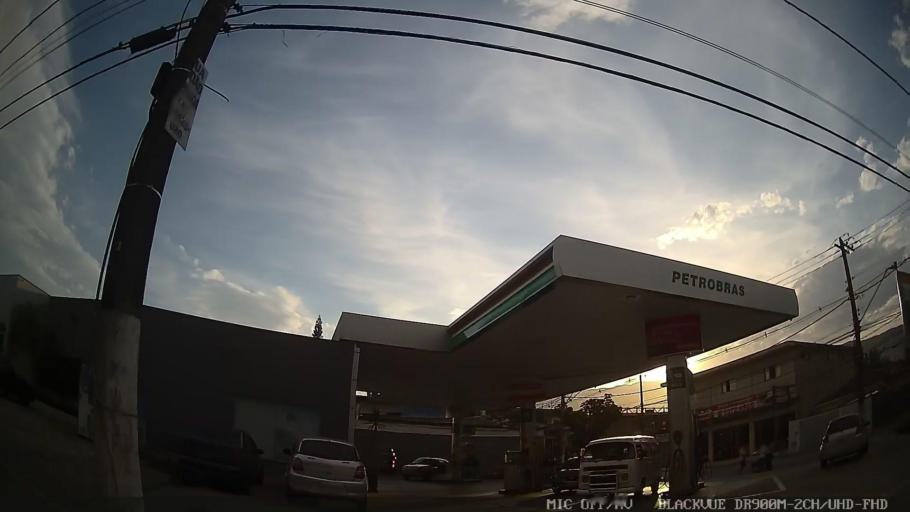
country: BR
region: Sao Paulo
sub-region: Cubatao
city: Cubatao
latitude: -23.8925
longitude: -46.4264
